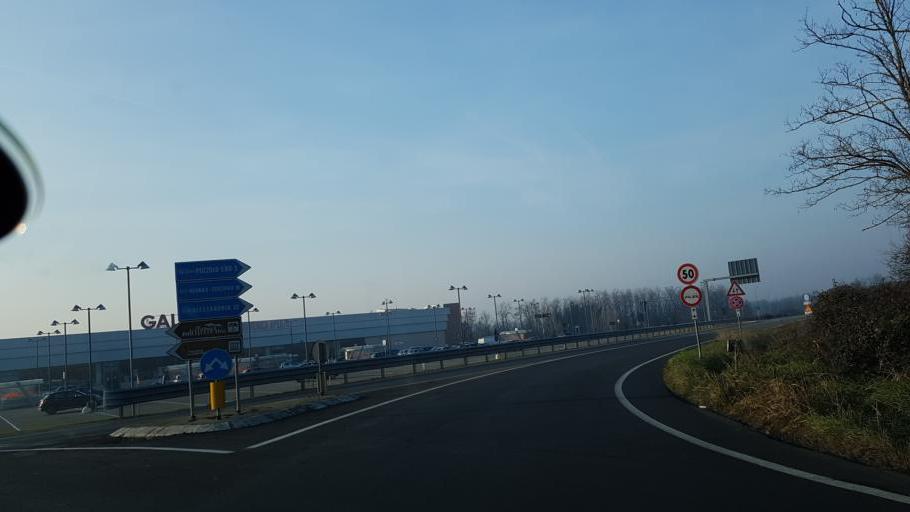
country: IT
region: Piedmont
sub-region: Provincia di Alessandria
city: Novi Ligure
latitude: 44.7725
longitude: 8.8013
